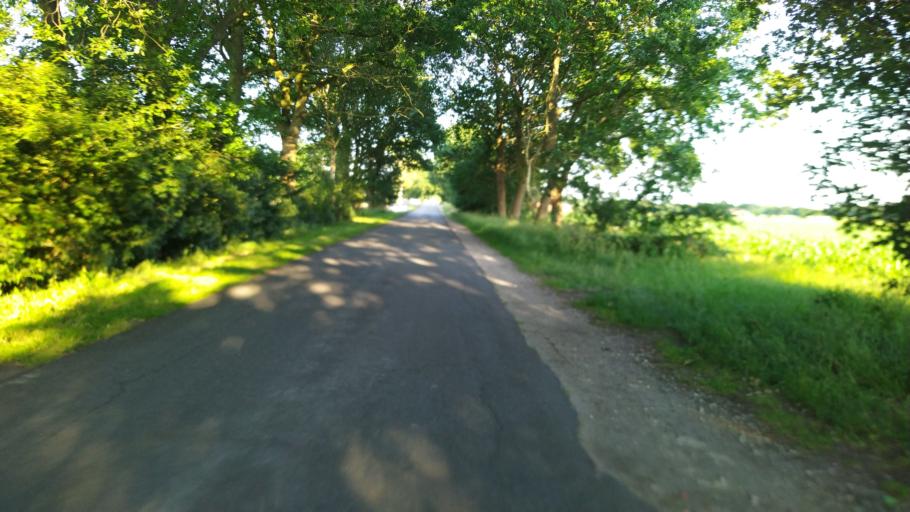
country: DE
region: Lower Saxony
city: Alfstedt
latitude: 53.5530
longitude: 9.0515
